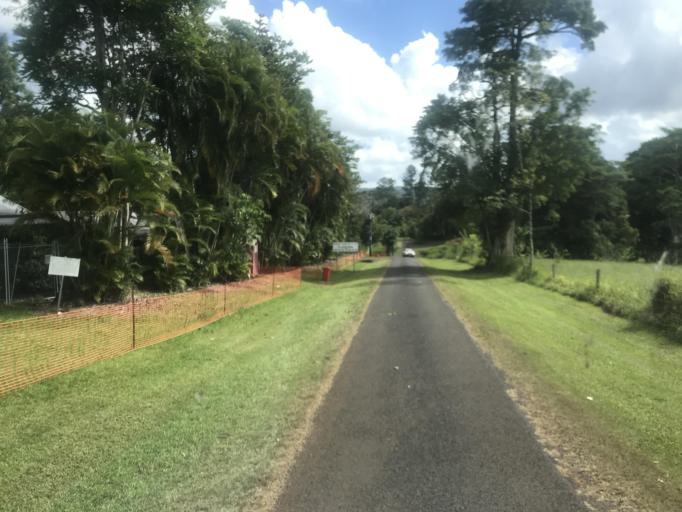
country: AU
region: Queensland
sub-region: Tablelands
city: Ravenshoe
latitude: -17.5493
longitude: 145.6978
